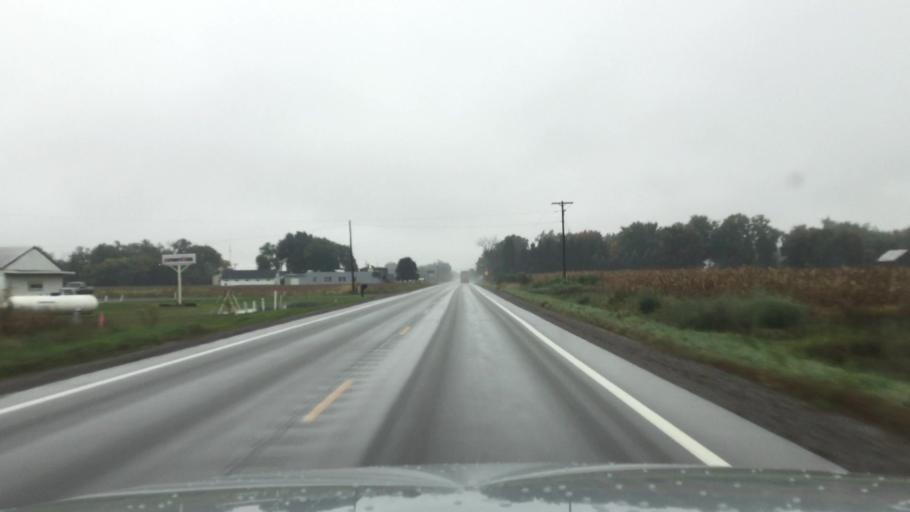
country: US
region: Michigan
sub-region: Saginaw County
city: Saginaw
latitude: 43.3548
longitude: -83.9546
